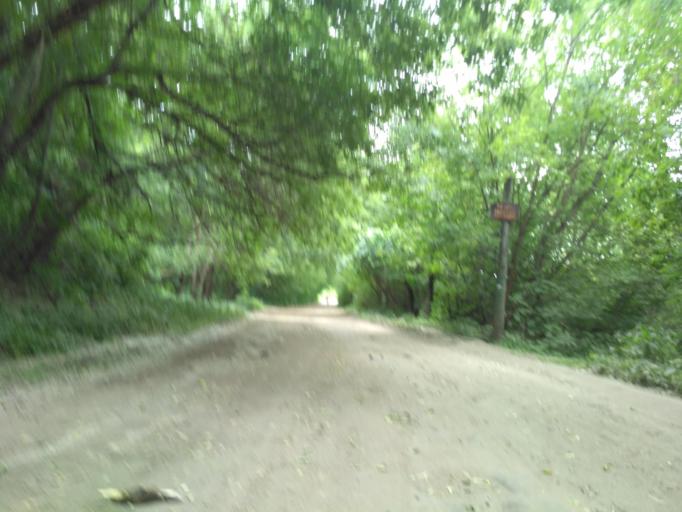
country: RU
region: Nizjnij Novgorod
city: Nizhniy Novgorod
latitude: 56.2902
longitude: 43.9684
